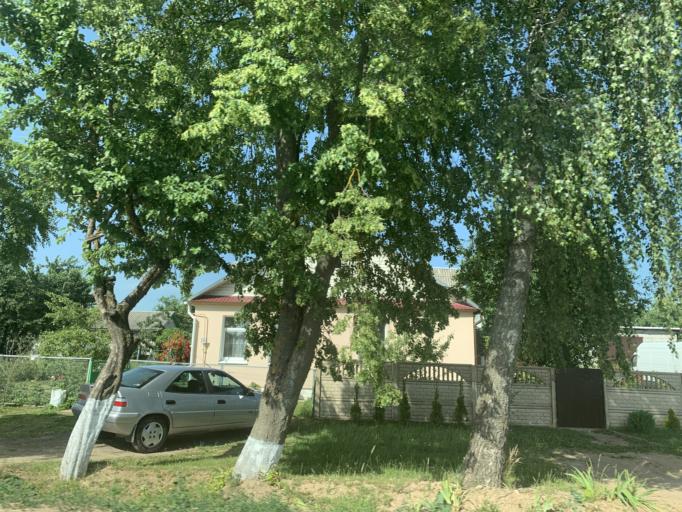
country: BY
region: Minsk
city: Dzyarzhynsk
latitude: 53.6997
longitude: 27.1001
